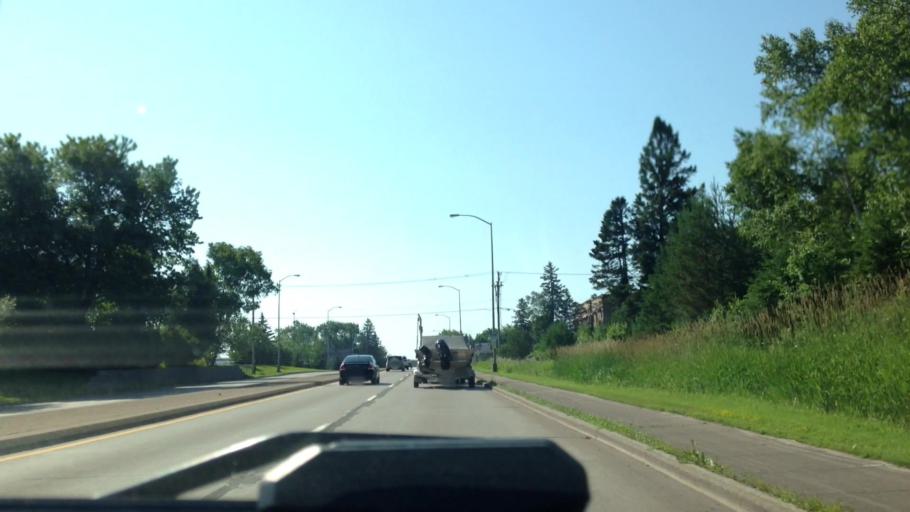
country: US
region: Wisconsin
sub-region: Douglas County
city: Superior
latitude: 46.6928
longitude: -92.0299
